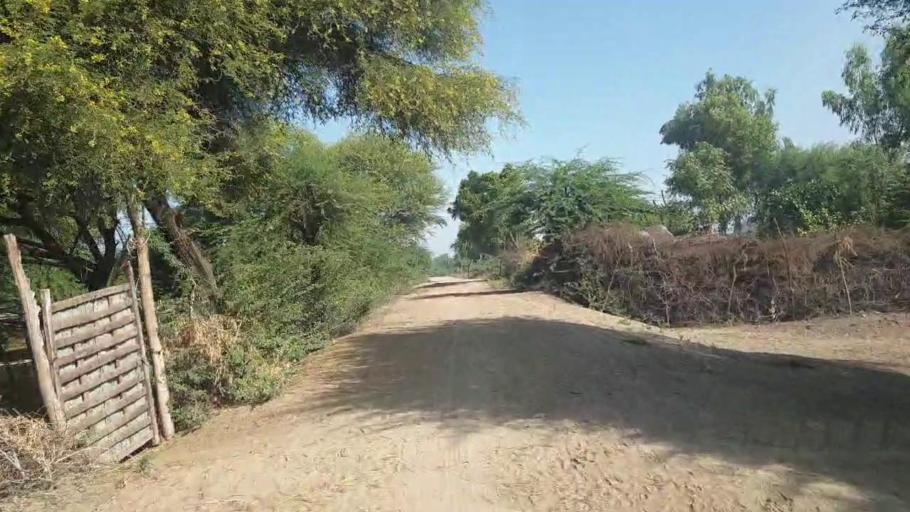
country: PK
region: Sindh
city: Talhar
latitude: 24.7831
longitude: 68.8082
